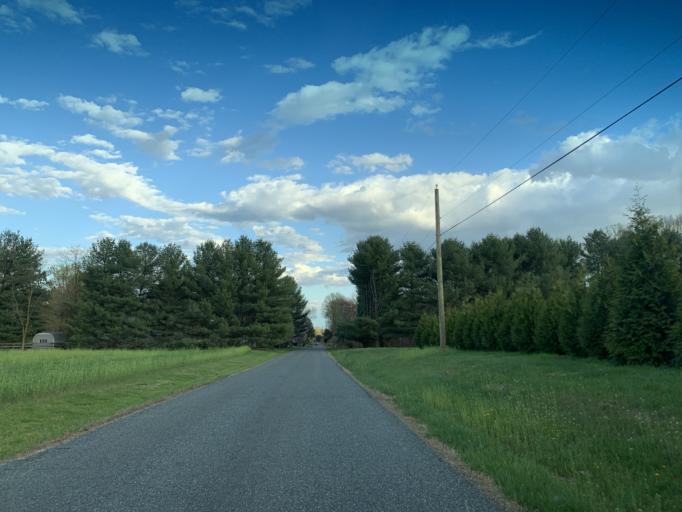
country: US
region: Maryland
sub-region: Harford County
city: South Bel Air
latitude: 39.5905
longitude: -76.3234
